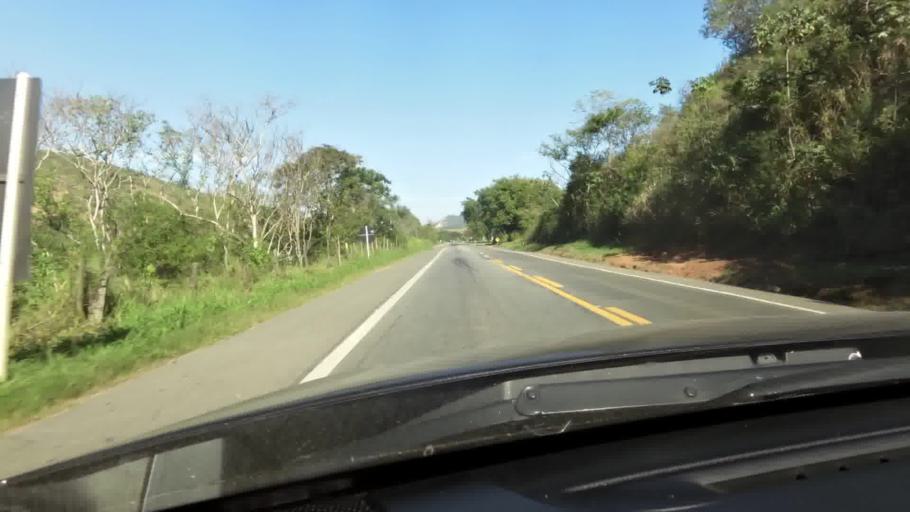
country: BR
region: Espirito Santo
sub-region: Cachoeiro De Itapemirim
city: Cachoeiro de Itapemirim
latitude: -20.9135
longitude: -41.0704
